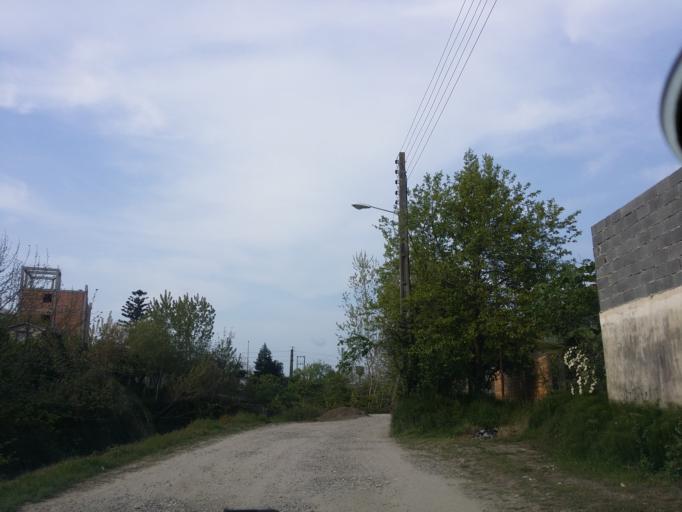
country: IR
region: Mazandaran
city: Chalus
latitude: 36.6849
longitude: 51.3968
